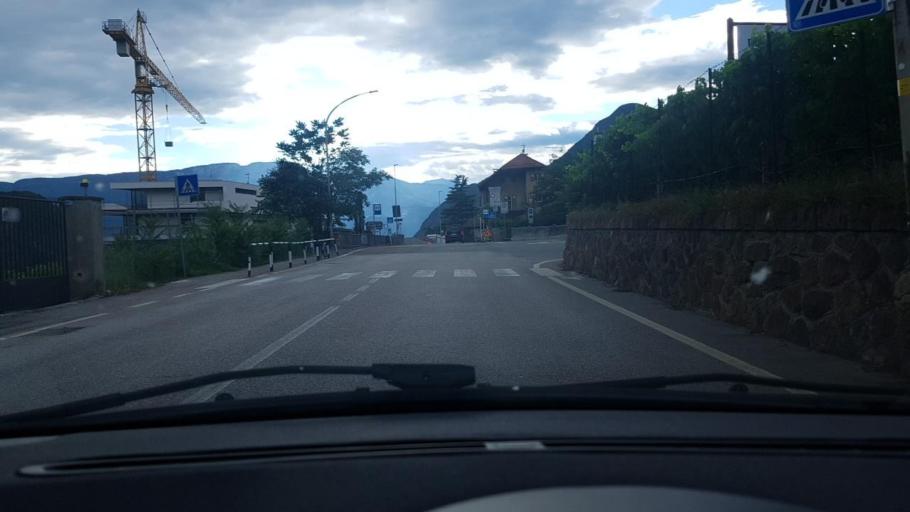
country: IT
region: Trentino-Alto Adige
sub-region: Bolzano
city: Cardano
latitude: 46.4971
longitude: 11.3805
